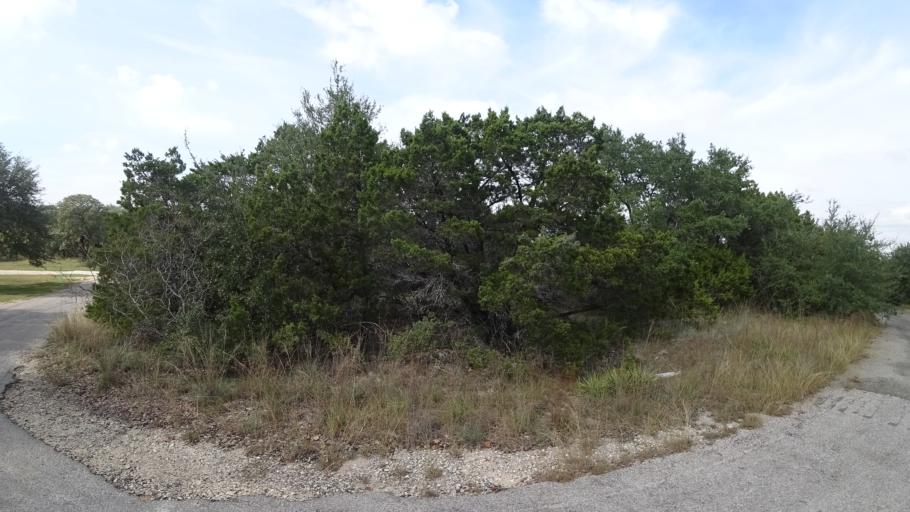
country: US
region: Texas
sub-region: Travis County
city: Hudson Bend
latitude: 30.3783
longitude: -97.9321
